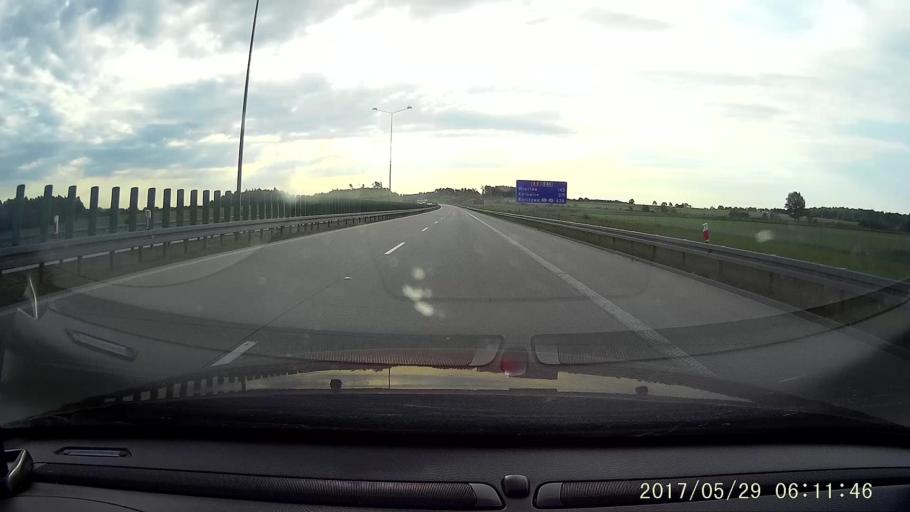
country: PL
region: Lower Silesian Voivodeship
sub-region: Powiat zgorzelecki
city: Wegliniec
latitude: 51.2164
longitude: 15.2508
